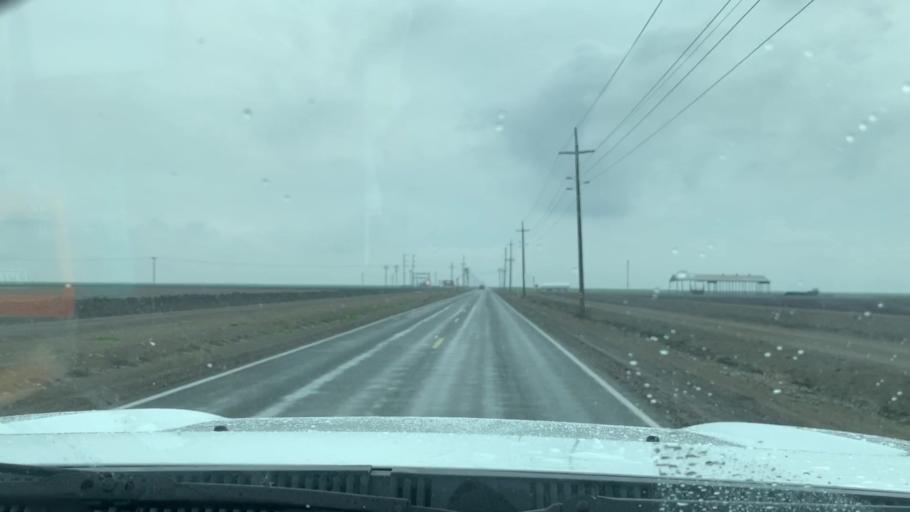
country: US
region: California
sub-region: Kings County
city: Corcoran
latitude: 35.9957
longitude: -119.5720
